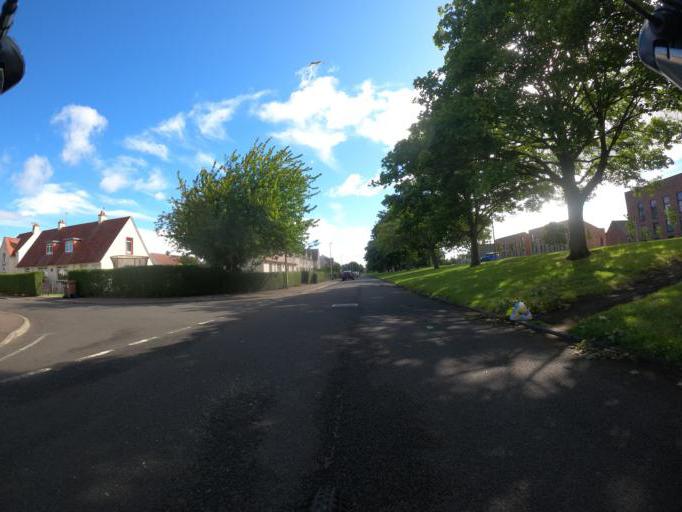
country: GB
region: Scotland
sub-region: Edinburgh
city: Edinburgh
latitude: 55.9745
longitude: -3.2583
